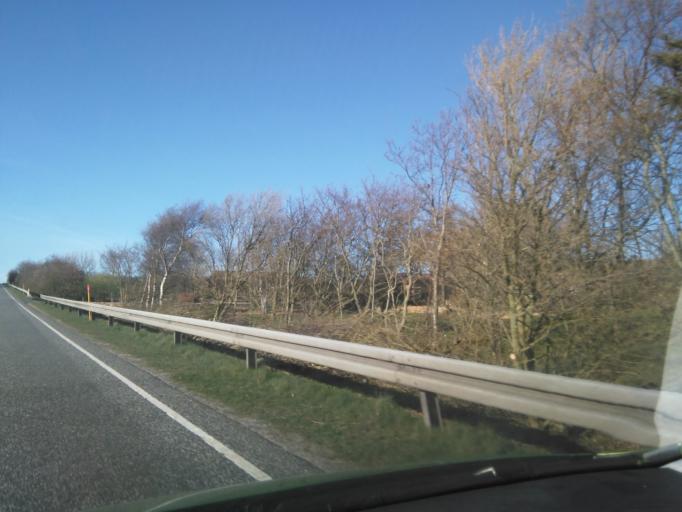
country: DK
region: Central Jutland
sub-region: Ringkobing-Skjern Kommune
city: Videbaek
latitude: 56.0764
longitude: 8.5071
